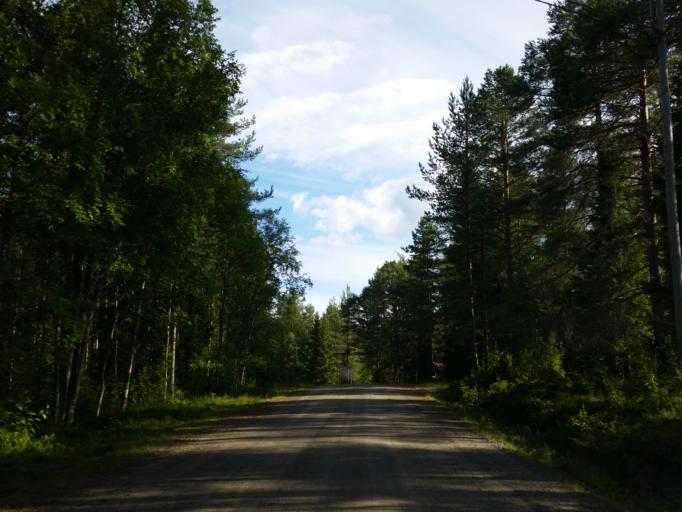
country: SE
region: Vaesterbotten
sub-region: Robertsfors Kommun
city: Robertsfors
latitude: 64.0406
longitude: 20.8500
